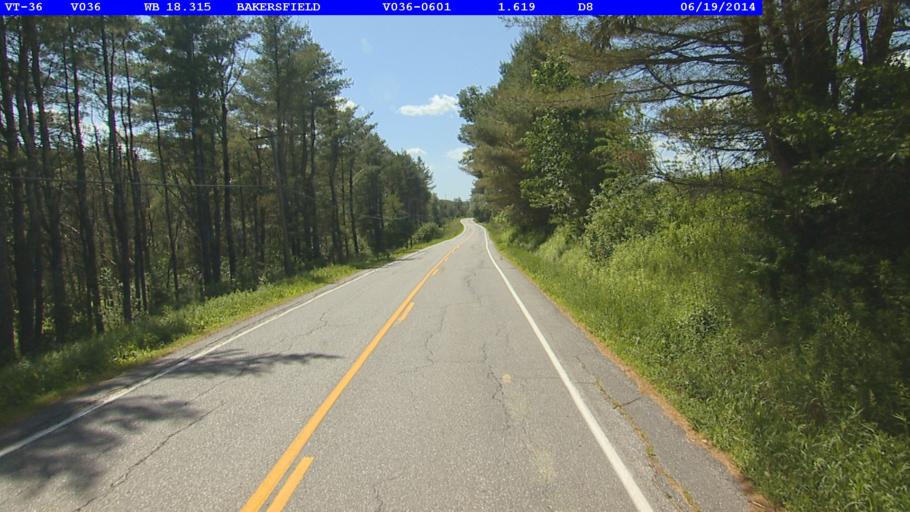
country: US
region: Vermont
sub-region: Franklin County
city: Enosburg Falls
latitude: 44.7811
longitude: -72.8186
